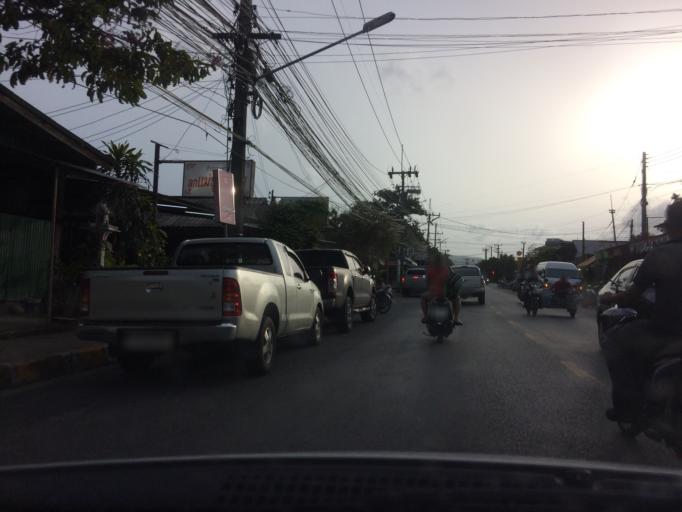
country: TH
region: Phuket
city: Ban Talat Yai
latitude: 7.8814
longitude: 98.4020
